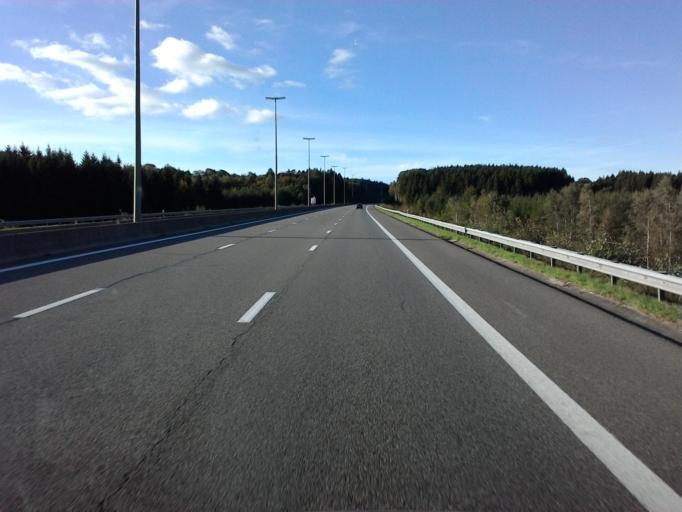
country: BE
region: Wallonia
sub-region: Province du Luxembourg
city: Houffalize
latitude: 50.1794
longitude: 5.7853
